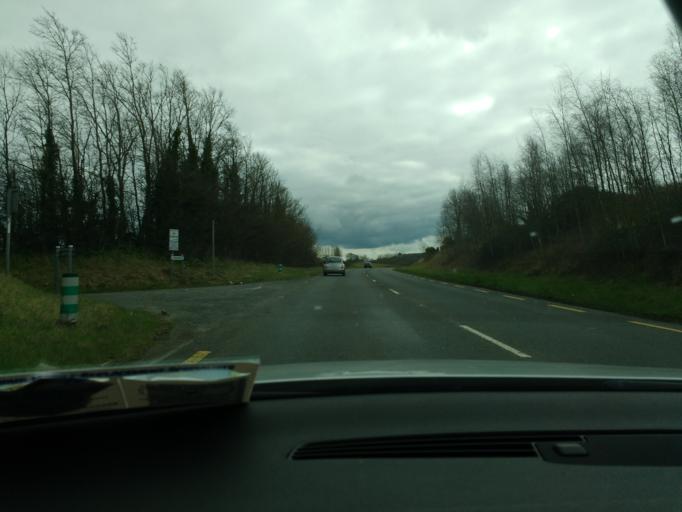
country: IE
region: Leinster
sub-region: Kilkenny
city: Ballyragget
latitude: 52.7163
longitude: -7.3330
